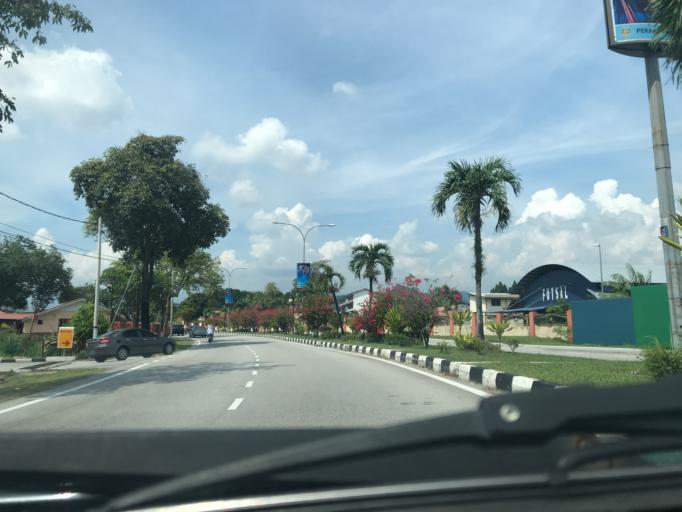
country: MY
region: Perak
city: Ipoh
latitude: 4.6011
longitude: 101.0994
